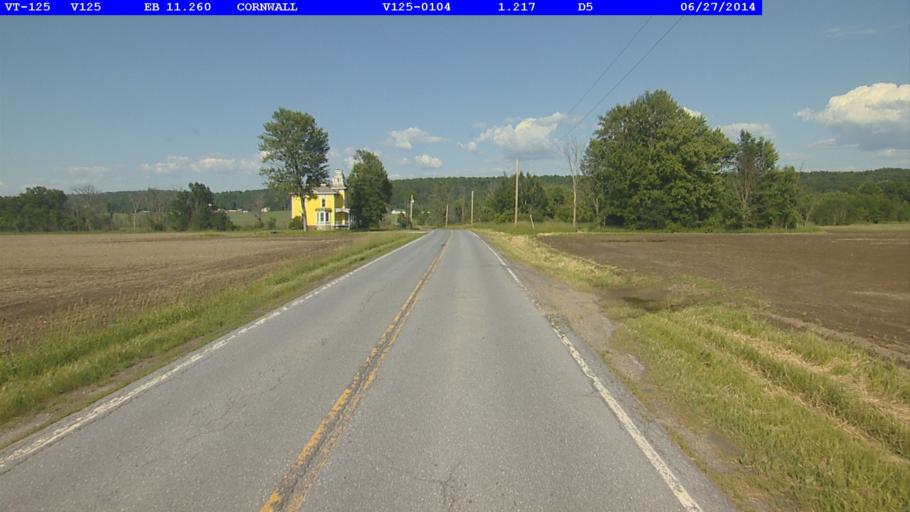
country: US
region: Vermont
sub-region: Addison County
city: Middlebury (village)
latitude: 43.9920
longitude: -73.2389
